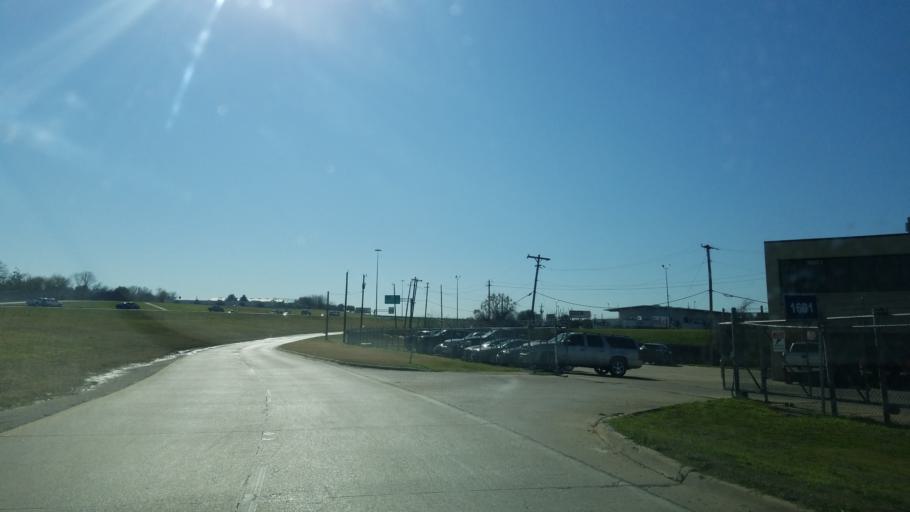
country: US
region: Texas
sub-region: Dallas County
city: Cockrell Hill
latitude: 32.7632
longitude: -96.9171
